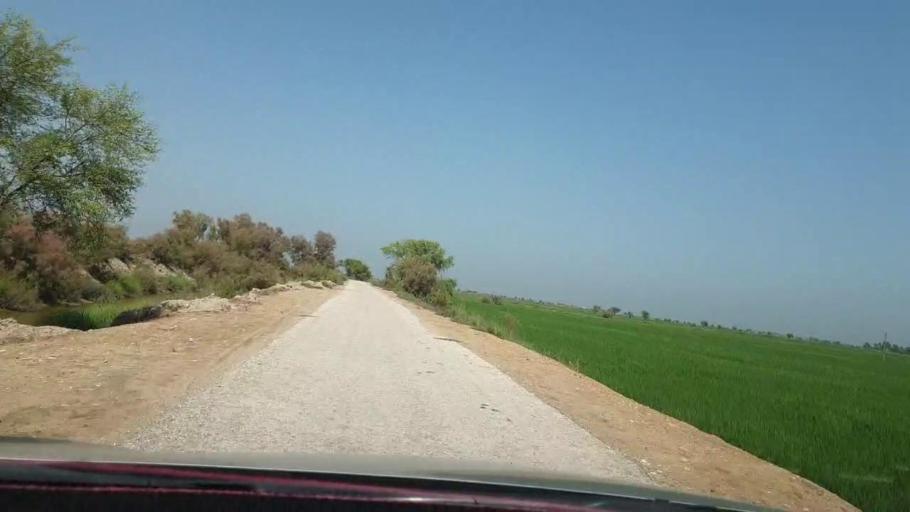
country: PK
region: Sindh
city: Warah
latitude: 27.5527
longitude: 67.7390
